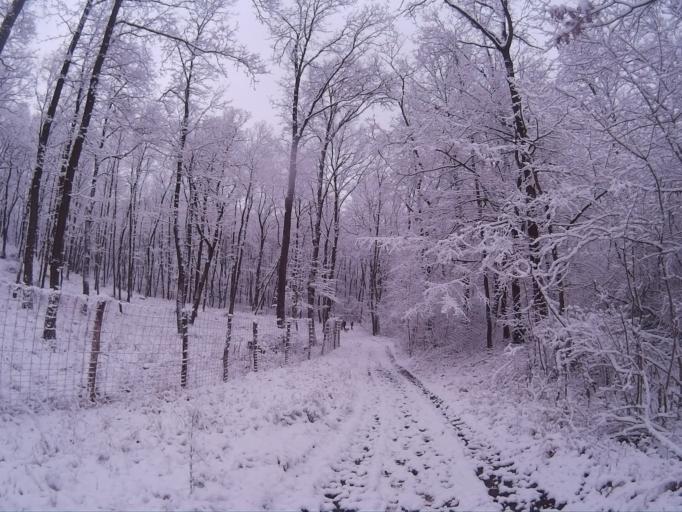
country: HU
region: Fejer
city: Szarliget
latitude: 47.5488
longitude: 18.5320
